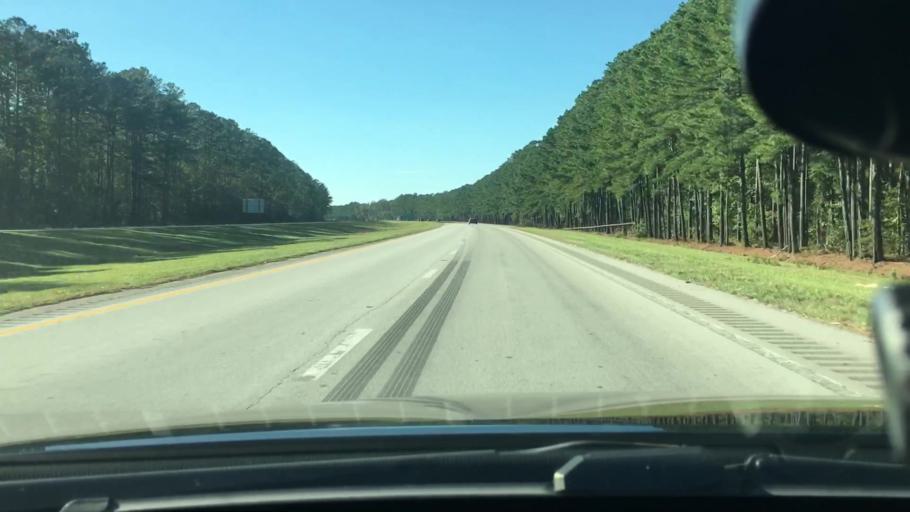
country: US
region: North Carolina
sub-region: Craven County
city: Trent Woods
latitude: 35.1170
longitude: -77.1040
